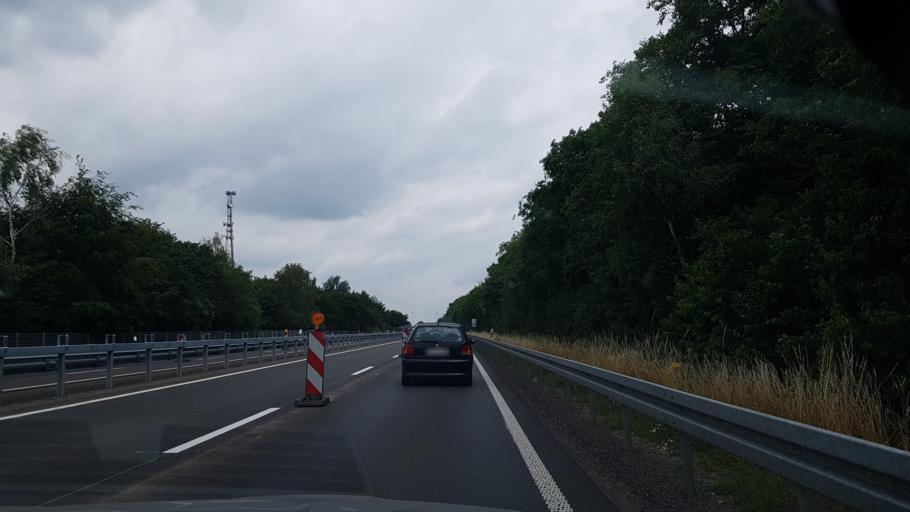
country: DE
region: Schleswig-Holstein
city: Neumunster
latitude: 54.1064
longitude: 9.9711
